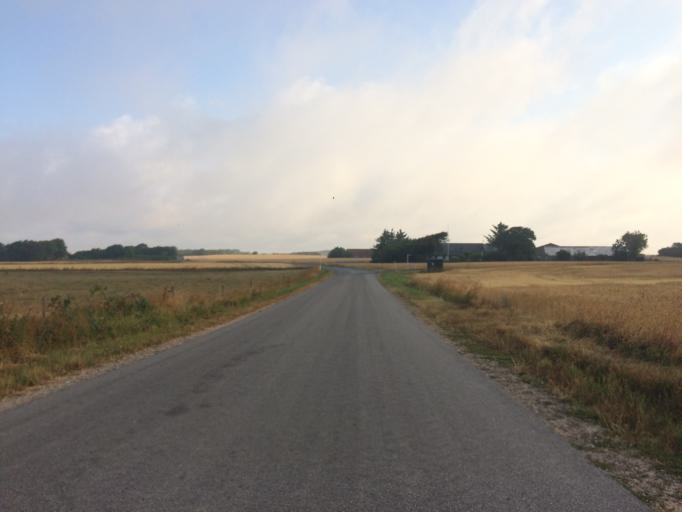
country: DK
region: Central Jutland
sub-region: Holstebro Kommune
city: Vinderup
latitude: 56.5803
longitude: 8.7583
